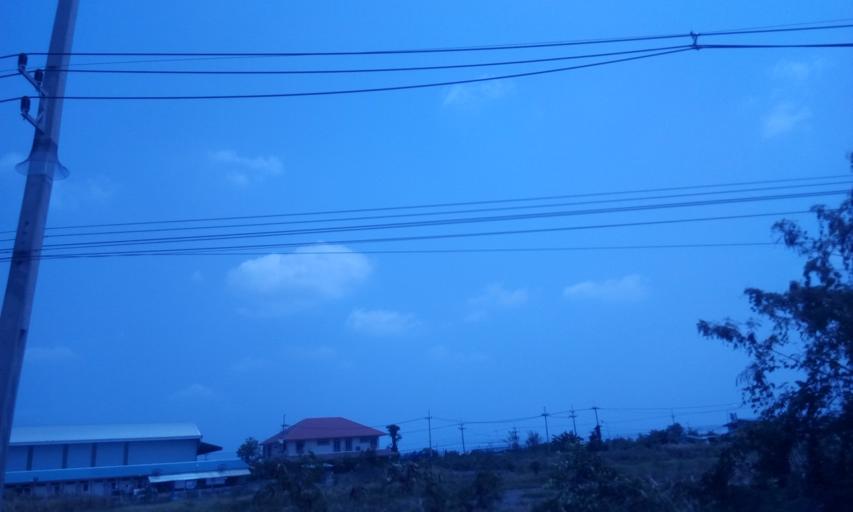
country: TH
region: Chachoengsao
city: Bang Nam Priao
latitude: 13.8329
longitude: 101.0557
